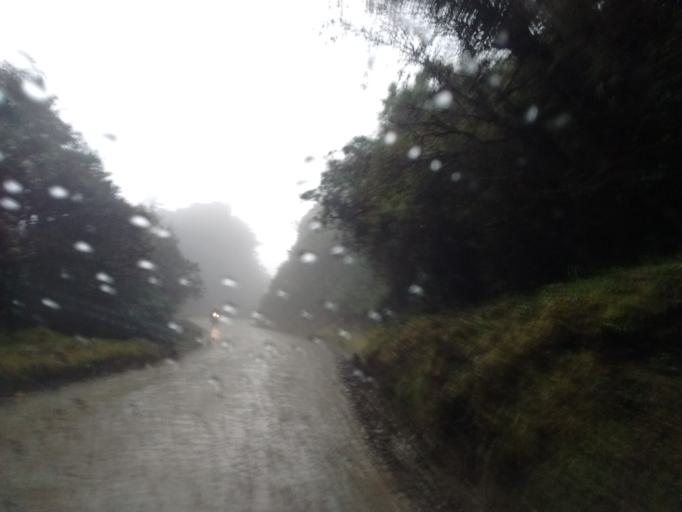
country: CO
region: Cauca
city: Paispamba
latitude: 2.1650
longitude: -76.4150
